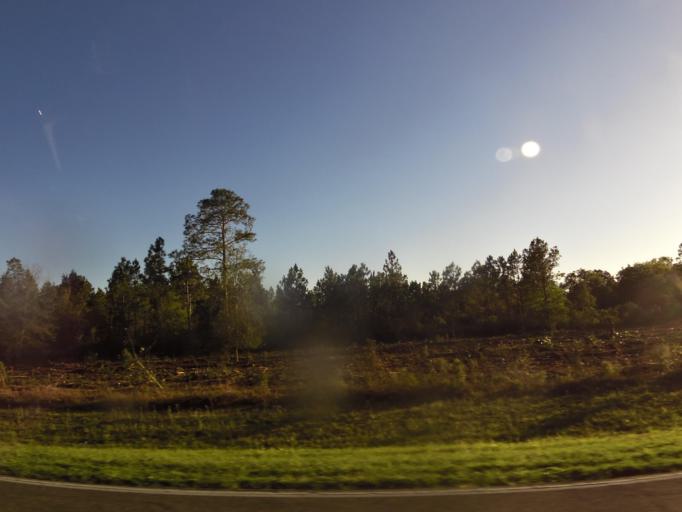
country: US
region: Florida
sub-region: Bradford County
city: Starke
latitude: 29.8540
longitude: -82.1018
